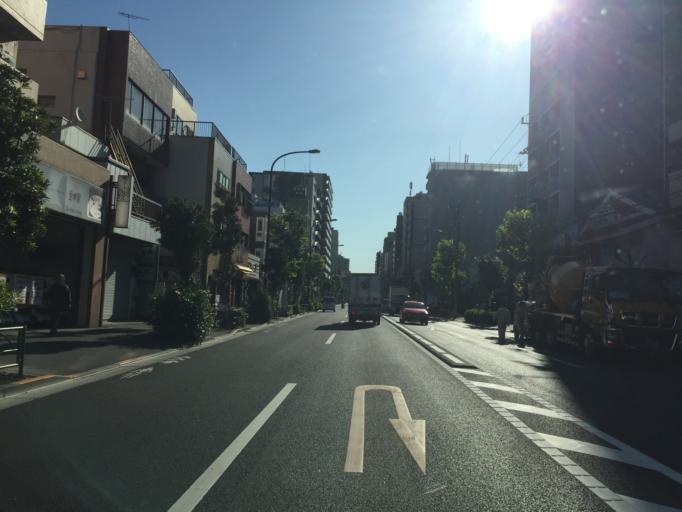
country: JP
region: Saitama
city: Kawaguchi
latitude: 35.7462
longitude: 139.7565
